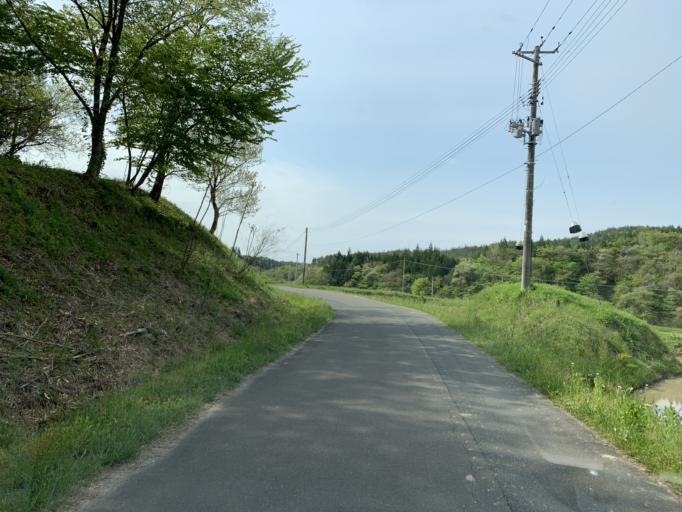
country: JP
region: Iwate
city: Ichinoseki
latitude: 38.9044
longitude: 141.0565
